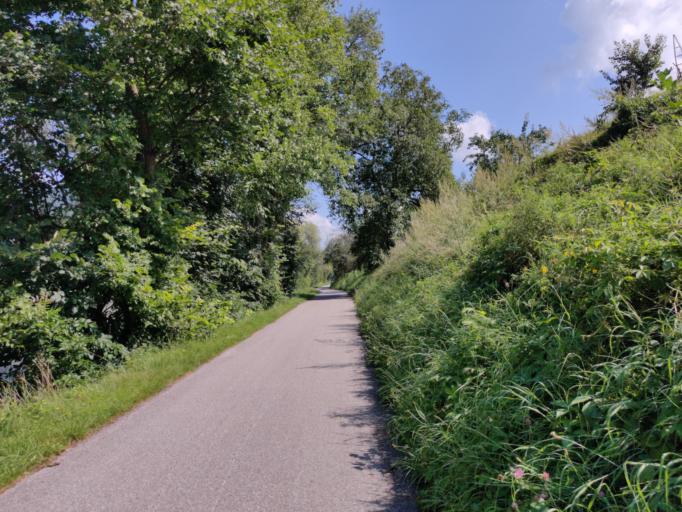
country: AT
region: Lower Austria
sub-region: Politischer Bezirk Krems
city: Spitz
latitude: 48.3586
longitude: 15.4172
